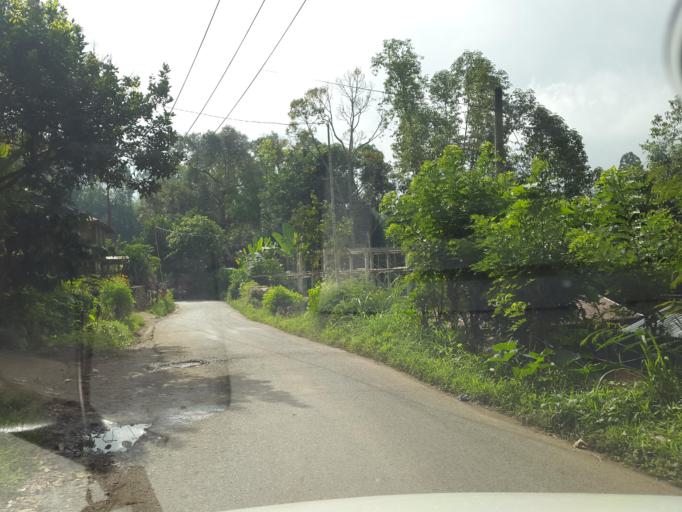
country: ID
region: South Sulawesi
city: Rantepao
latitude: -3.0181
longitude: 119.8565
